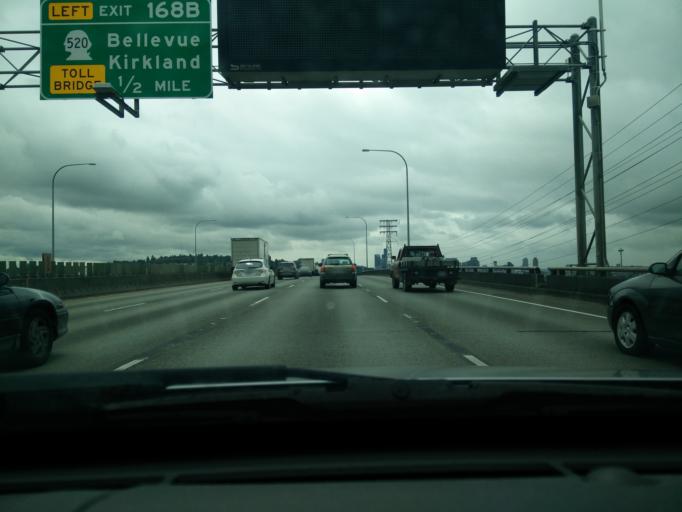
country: US
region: Washington
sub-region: King County
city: Seattle
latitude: 47.6541
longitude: -122.3226
